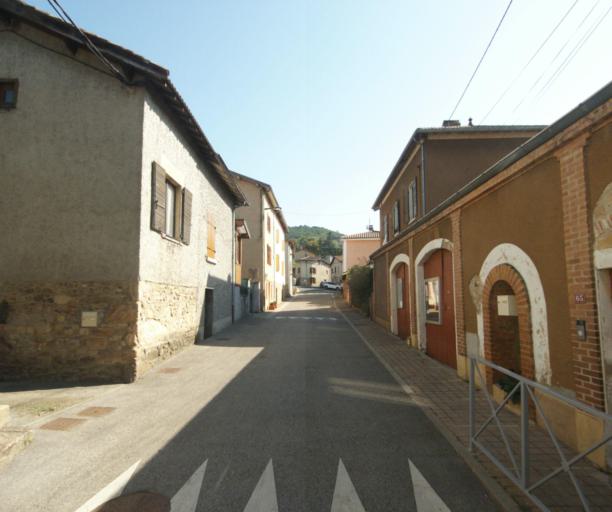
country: FR
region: Rhone-Alpes
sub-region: Departement du Rhone
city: Saint-Pierre-la-Palud
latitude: 45.7712
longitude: 4.6078
